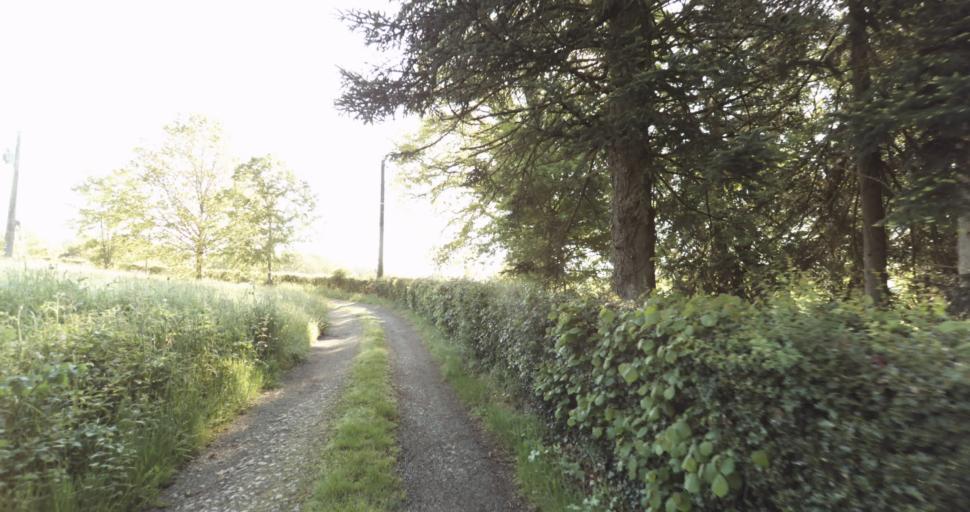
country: FR
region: Limousin
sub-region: Departement de la Haute-Vienne
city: Solignac
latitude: 45.7404
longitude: 1.2775
